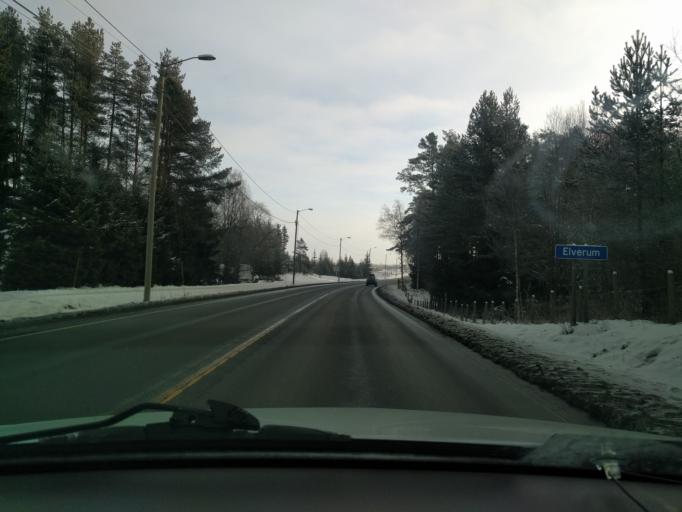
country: NO
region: Hedmark
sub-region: Elverum
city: Elverum
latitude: 60.8842
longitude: 11.5172
